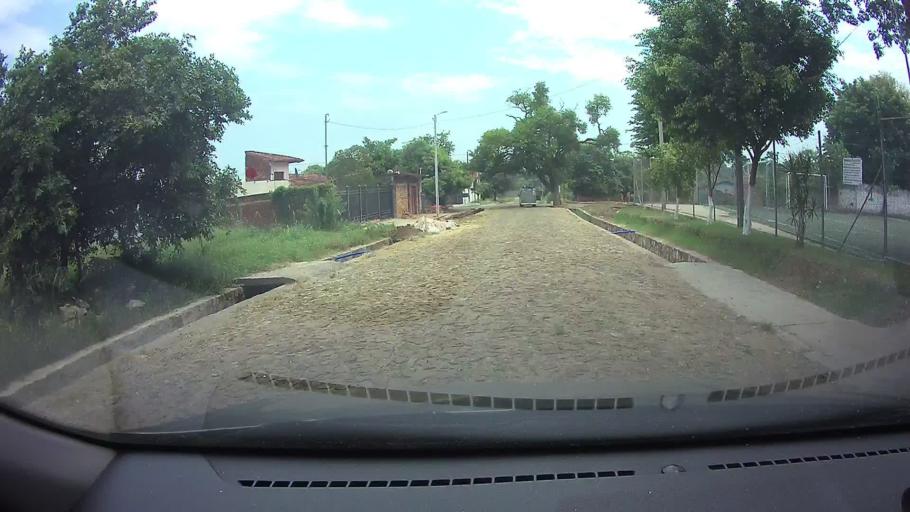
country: PY
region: Central
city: San Lorenzo
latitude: -25.2671
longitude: -57.4754
